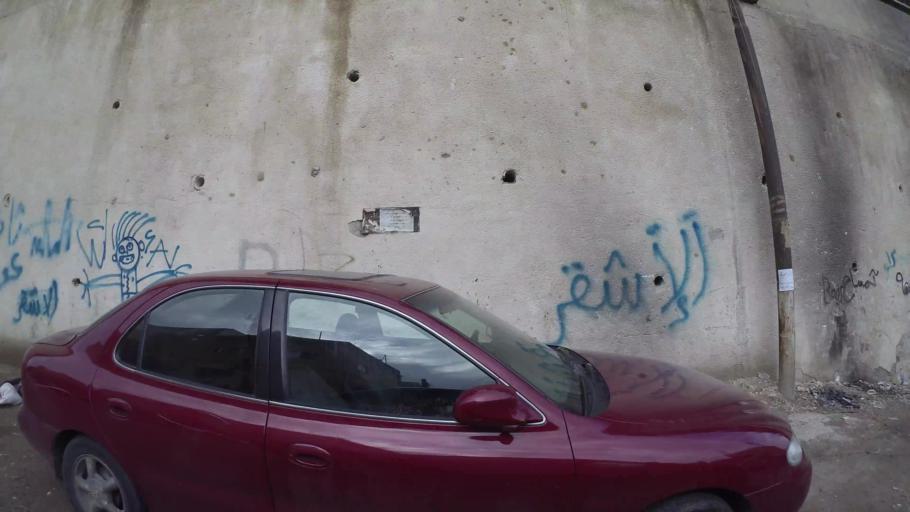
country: JO
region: Amman
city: Amman
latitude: 31.9635
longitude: 35.9325
